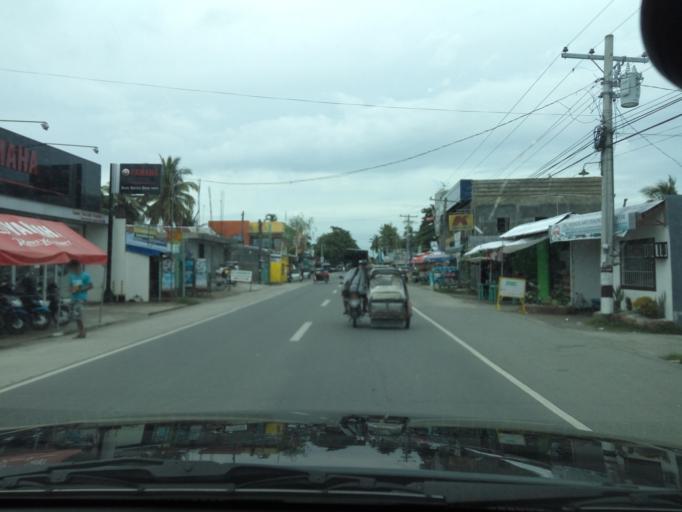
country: PH
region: Central Luzon
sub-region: Province of Nueva Ecija
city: Concepcion
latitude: 15.4490
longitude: 120.8012
